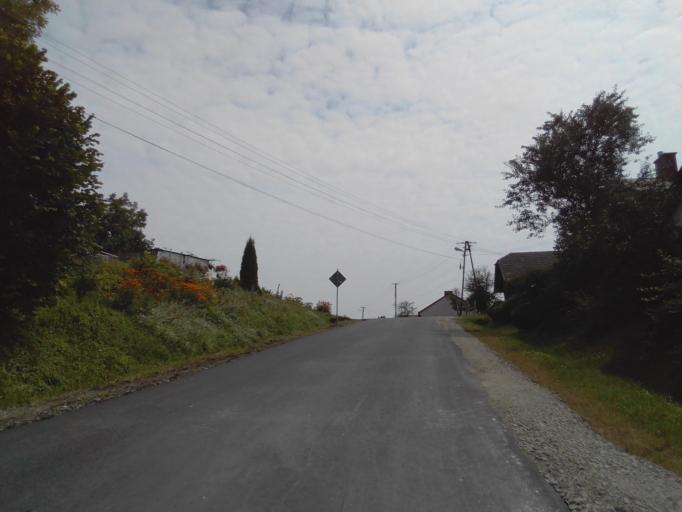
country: PL
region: Subcarpathian Voivodeship
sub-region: Powiat jasielski
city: Tarnowiec
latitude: 49.7734
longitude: 21.5820
